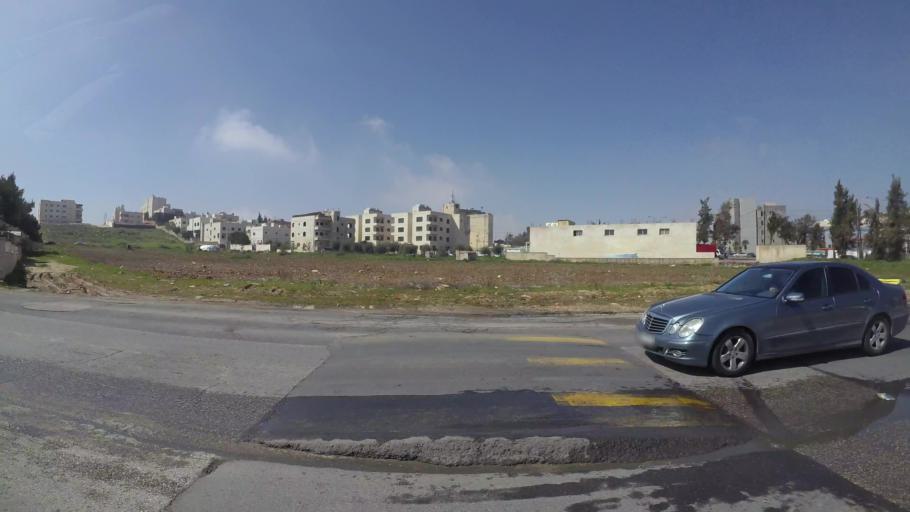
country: JO
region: Amman
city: Al Bunayyat ash Shamaliyah
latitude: 31.9013
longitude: 35.8742
